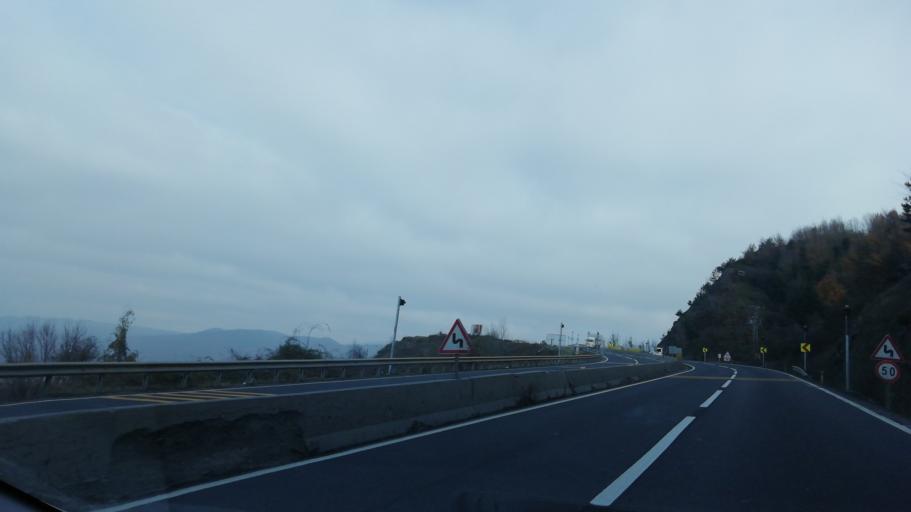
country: TR
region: Duzce
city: Kaynasli
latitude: 40.7531
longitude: 31.3876
